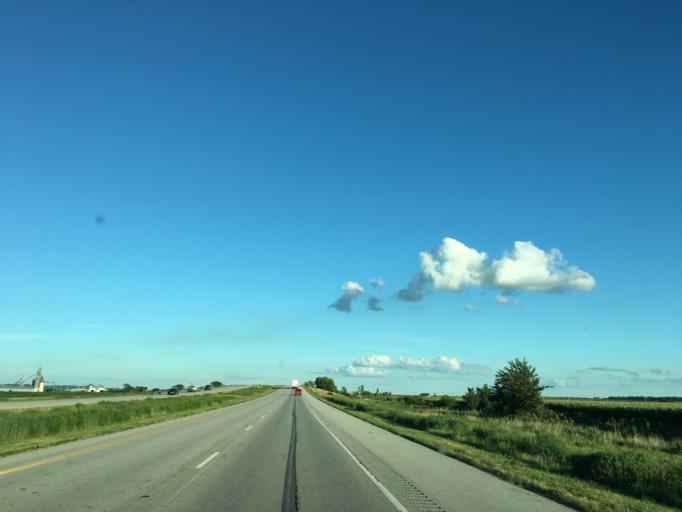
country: US
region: Nebraska
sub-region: Otoe County
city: Nebraska City
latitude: 40.6736
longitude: -95.7699
